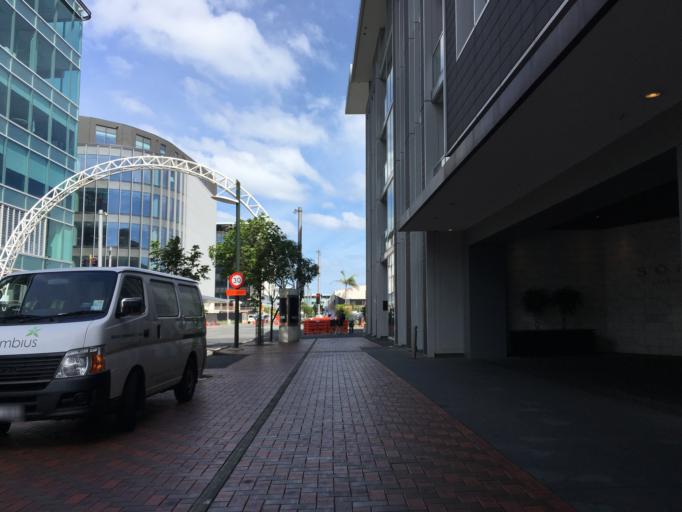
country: NZ
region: Auckland
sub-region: Auckland
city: Auckland
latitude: -36.8449
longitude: 174.7575
